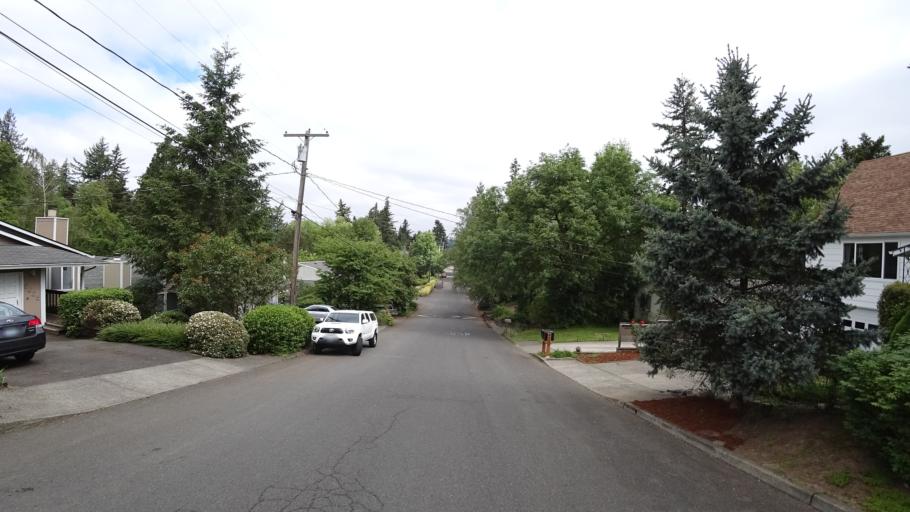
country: US
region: Oregon
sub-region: Washington County
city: Garden Home-Whitford
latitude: 45.4555
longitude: -122.7284
